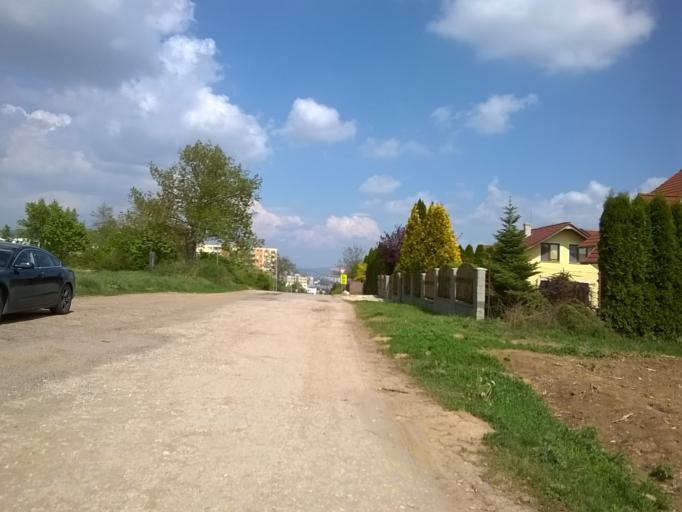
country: SK
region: Nitriansky
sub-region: Okres Nitra
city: Nitra
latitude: 48.2928
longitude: 18.0591
